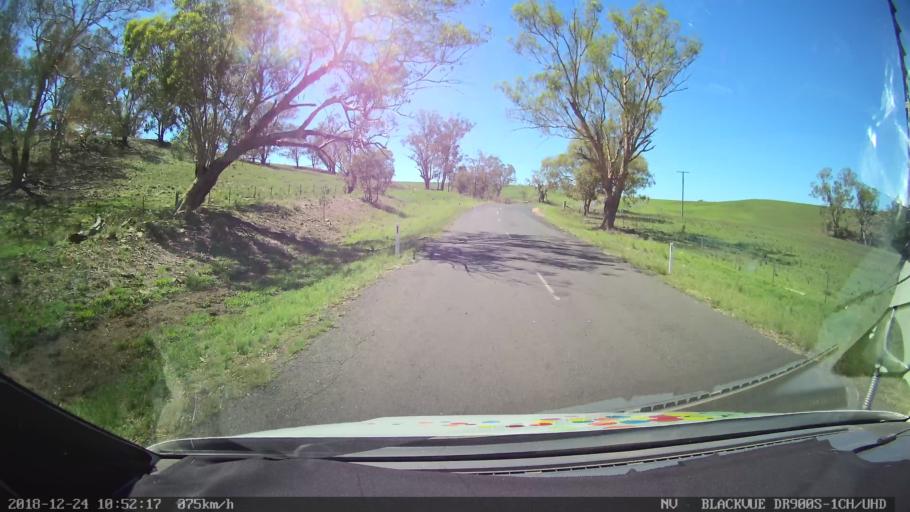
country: AU
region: New South Wales
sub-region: Upper Hunter Shire
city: Merriwa
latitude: -31.9788
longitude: 150.4217
